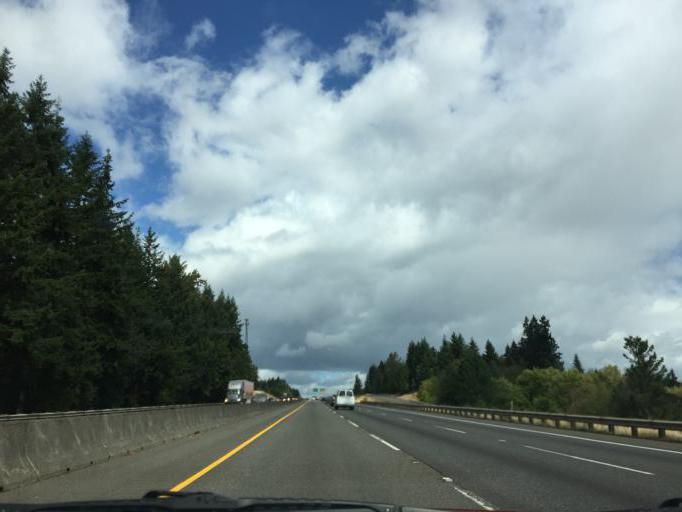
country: US
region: Washington
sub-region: Lewis County
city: Winlock
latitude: 46.4280
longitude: -122.8902
